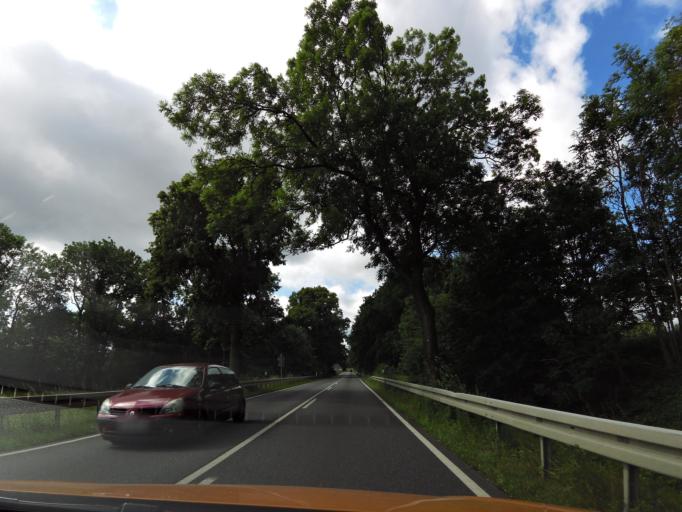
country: DE
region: Mecklenburg-Vorpommern
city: Krakow am See
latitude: 53.7010
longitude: 12.2770
